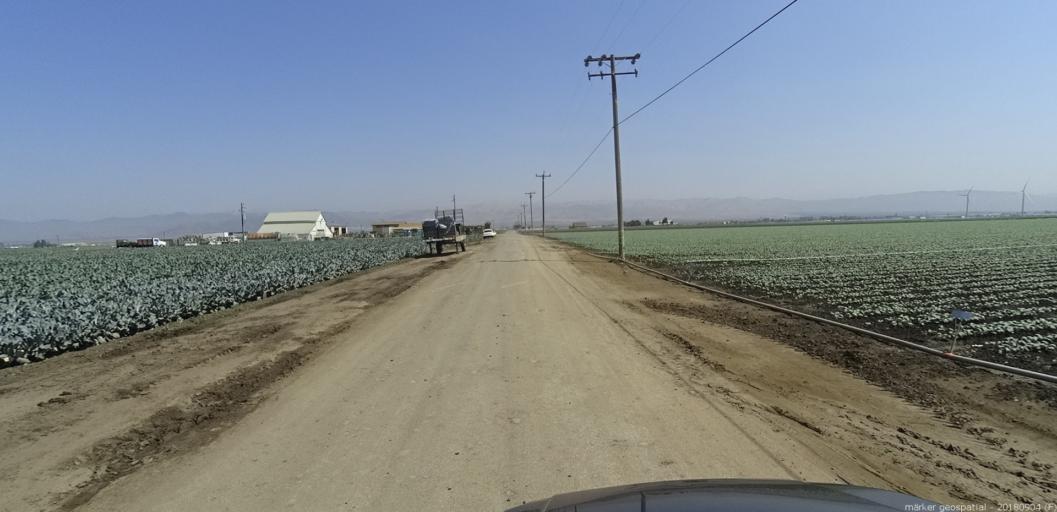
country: US
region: California
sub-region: Monterey County
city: Gonzales
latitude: 36.5078
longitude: -121.4765
